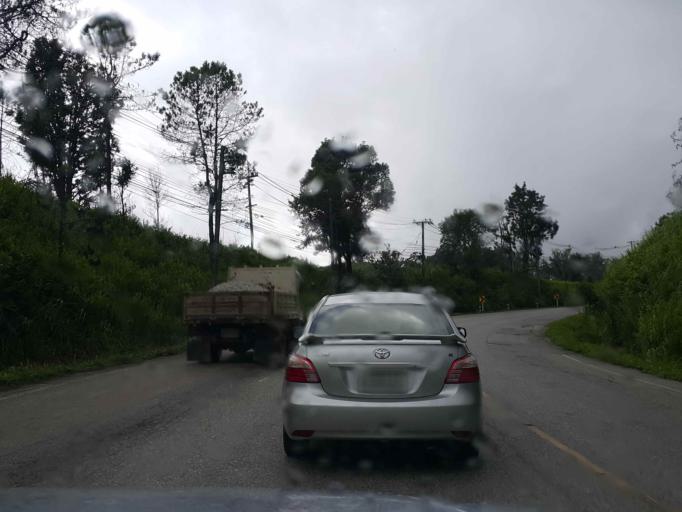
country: TH
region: Tak
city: Tak
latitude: 16.7730
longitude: 98.9360
